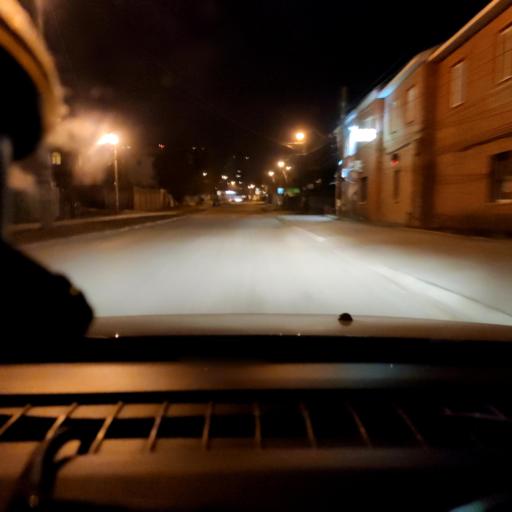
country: RU
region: Samara
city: Samara
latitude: 53.1910
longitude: 50.2152
